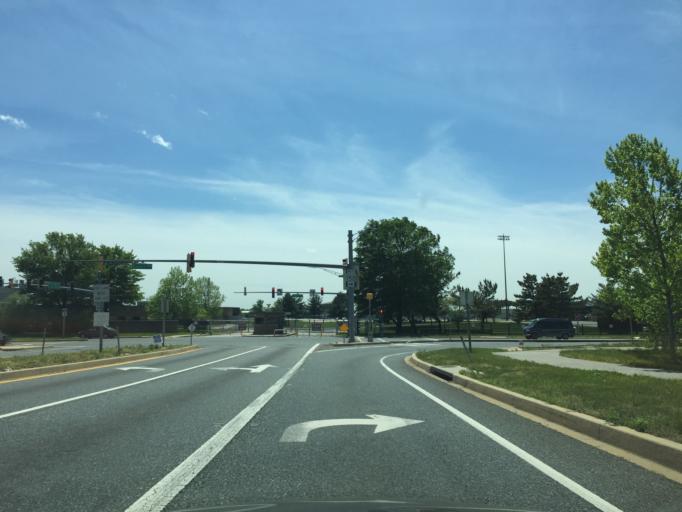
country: US
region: Maryland
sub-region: Baltimore County
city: Middle River
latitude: 39.3374
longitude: -76.4184
